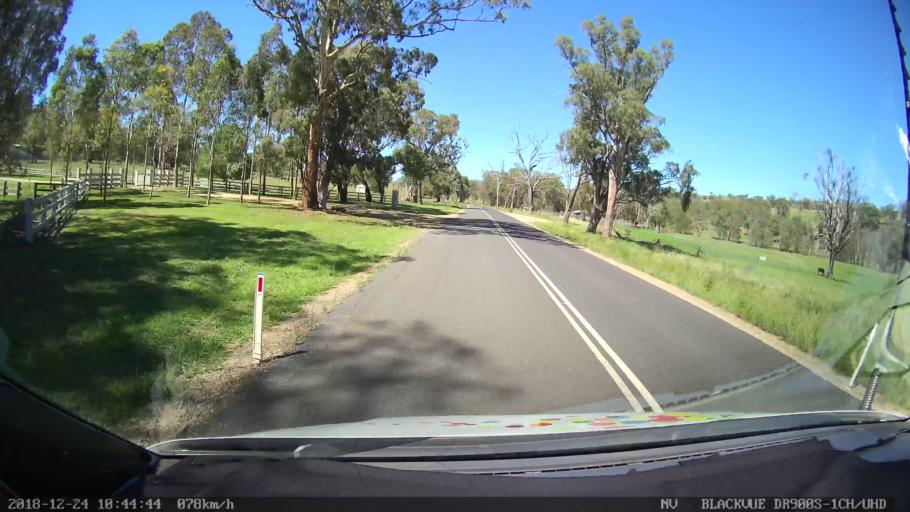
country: AU
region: New South Wales
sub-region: Upper Hunter Shire
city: Merriwa
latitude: -31.8960
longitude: 150.4416
